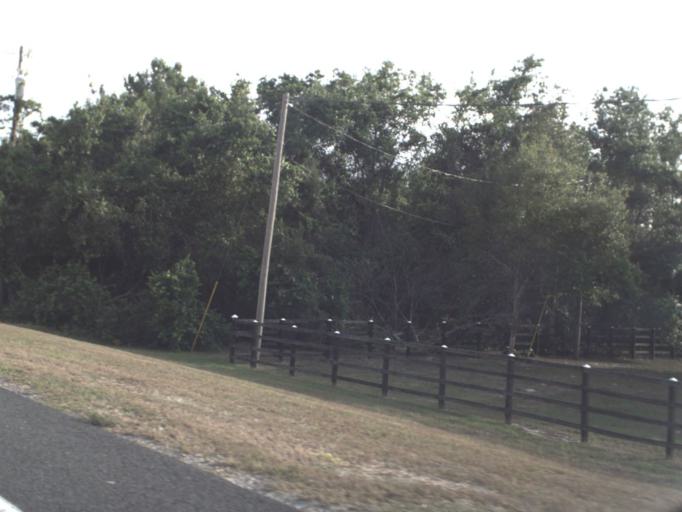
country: US
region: Florida
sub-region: Brevard County
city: Mims
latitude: 28.7373
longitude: -80.8686
